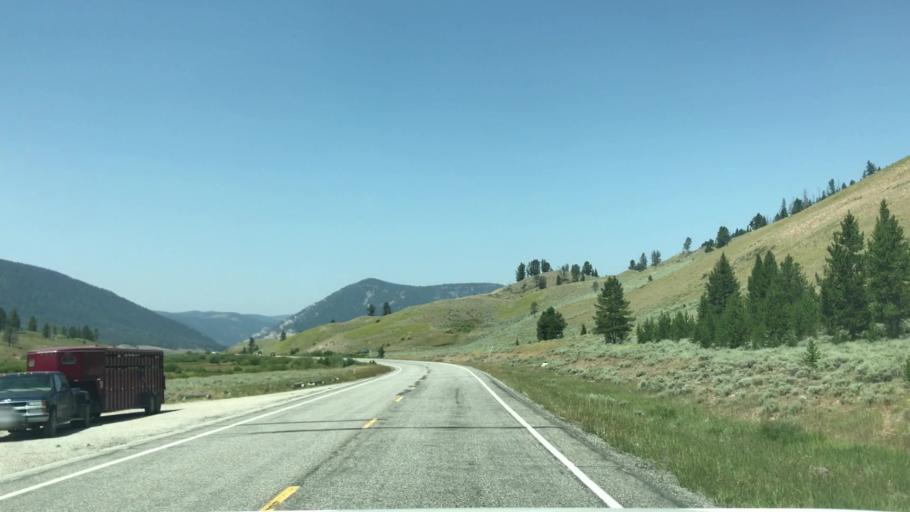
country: US
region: Montana
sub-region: Gallatin County
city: Big Sky
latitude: 45.0378
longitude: -111.1182
